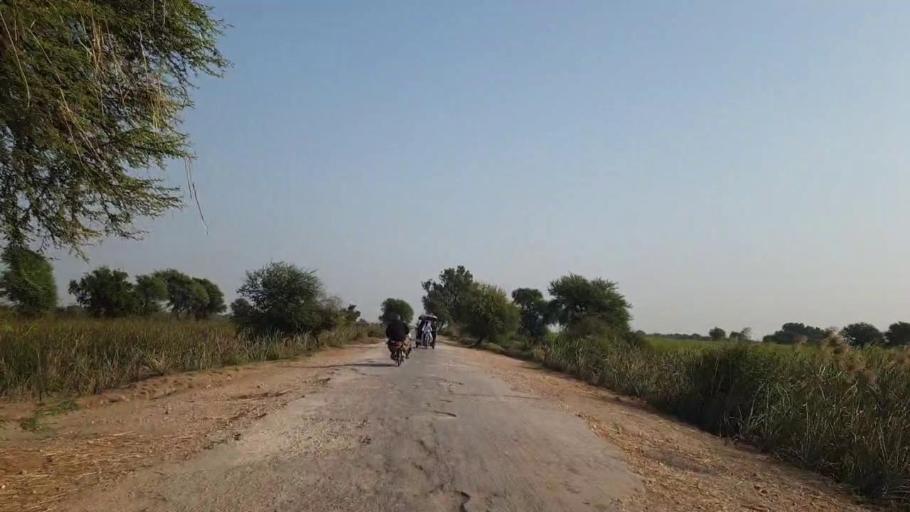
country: PK
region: Sindh
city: Bulri
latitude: 24.9759
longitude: 68.3983
